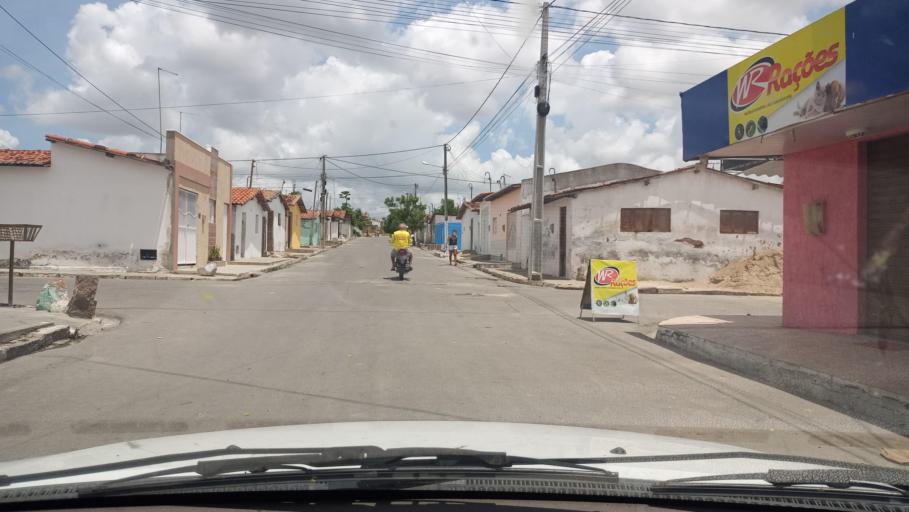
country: BR
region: Rio Grande do Norte
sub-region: Tangara
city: Tangara
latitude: -6.1013
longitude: -35.7101
